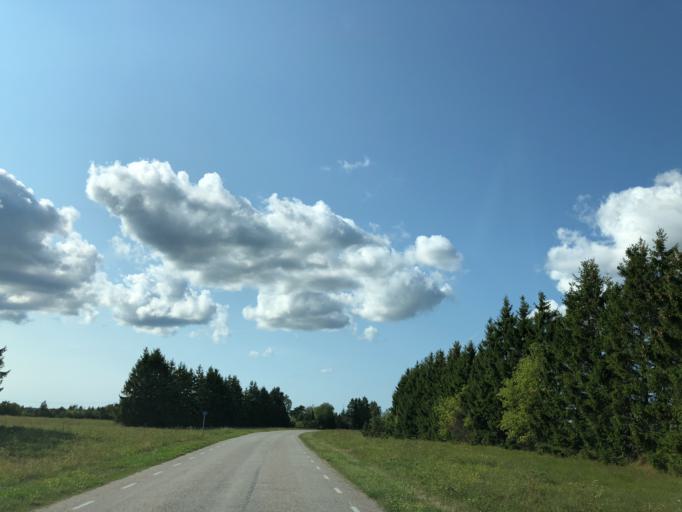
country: EE
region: Hiiumaa
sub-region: Kaerdla linn
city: Kardla
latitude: 58.7858
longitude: 22.7818
